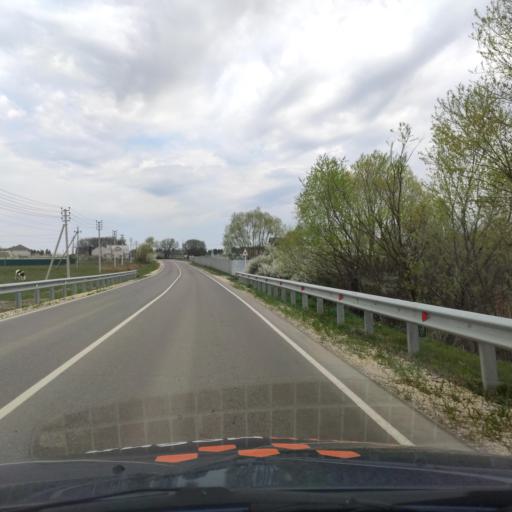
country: RU
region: Voronezj
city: Podgornoye
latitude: 51.8698
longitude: 39.1724
